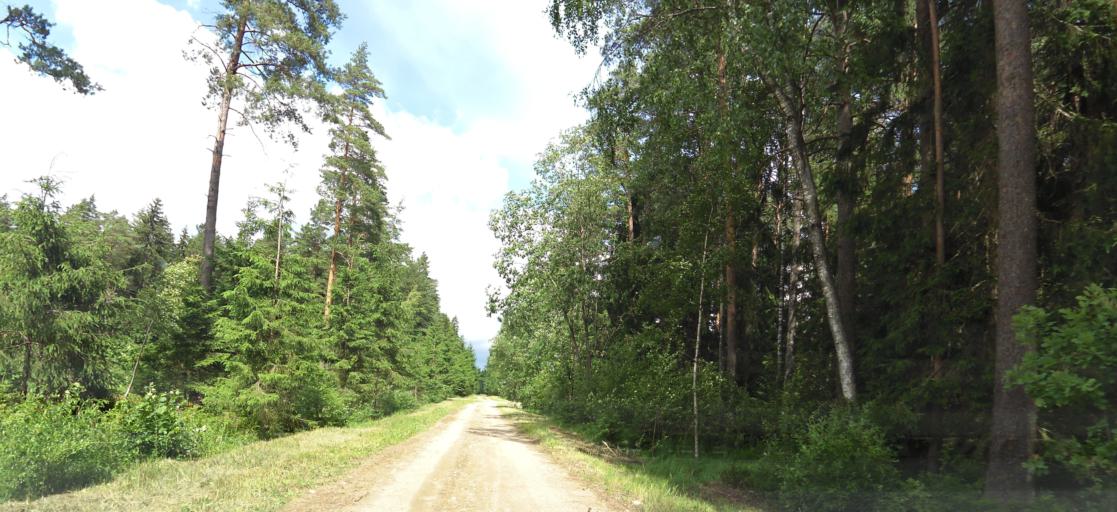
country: LT
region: Panevezys
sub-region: Birzai
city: Birzai
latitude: 56.2680
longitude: 24.7520
